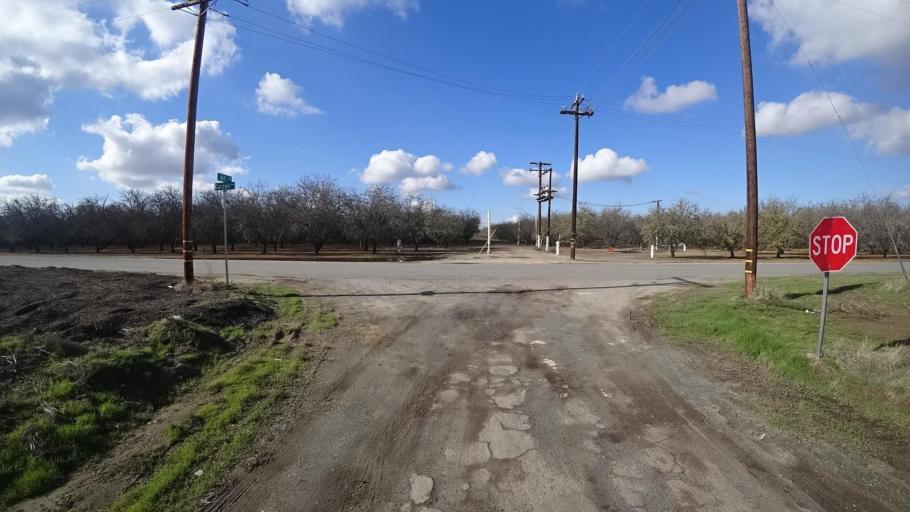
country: US
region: California
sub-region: Kern County
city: McFarland
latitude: 35.6526
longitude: -119.2409
